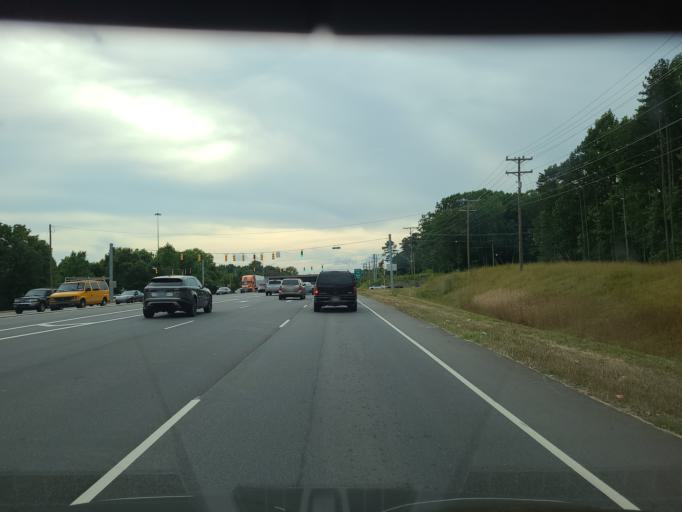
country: US
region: North Carolina
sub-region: Gaston County
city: Belmont
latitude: 35.2391
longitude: -80.9663
